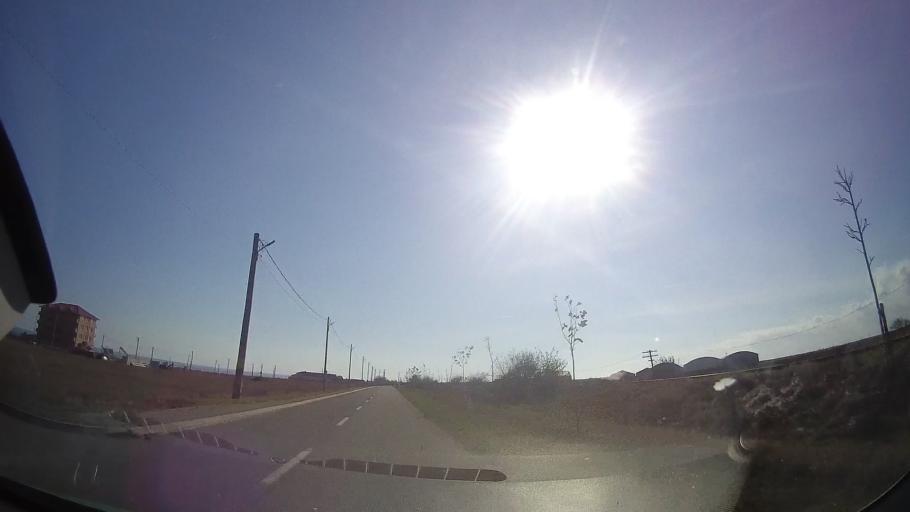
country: RO
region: Constanta
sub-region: Comuna Costinesti
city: Schitu
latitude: 43.9282
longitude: 28.6321
